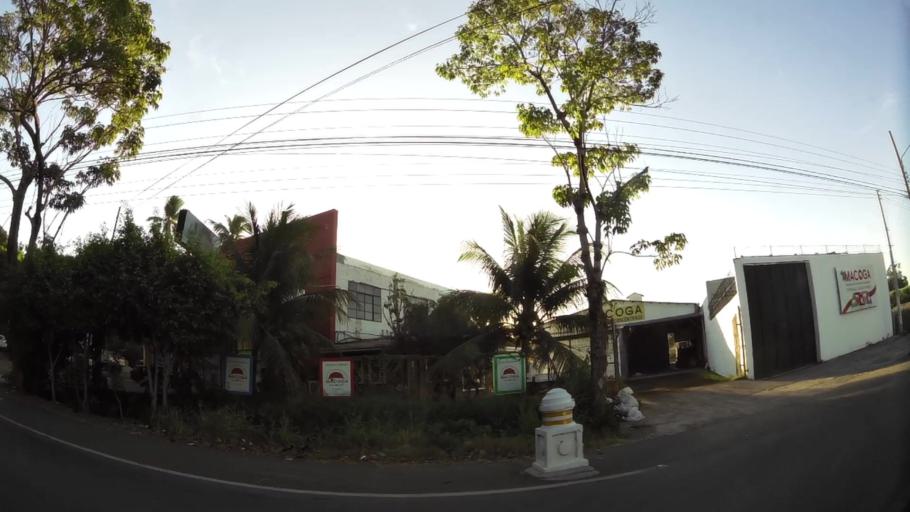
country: SV
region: Sonsonate
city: Sonsonate
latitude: 13.7088
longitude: -89.7294
